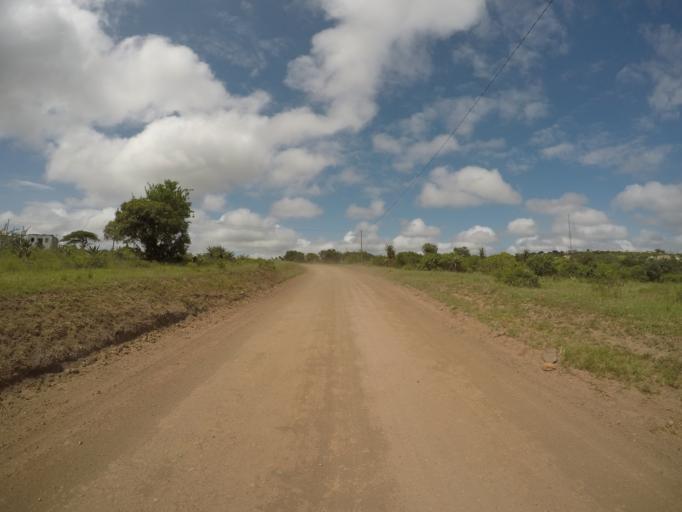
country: ZA
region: KwaZulu-Natal
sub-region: uThungulu District Municipality
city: Empangeni
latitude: -28.6012
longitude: 31.8387
